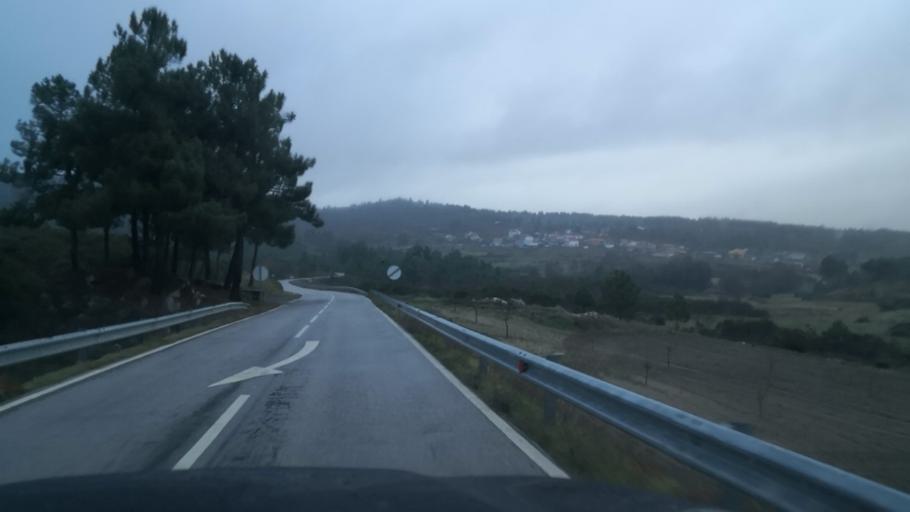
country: PT
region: Vila Real
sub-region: Murca
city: Murca
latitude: 41.4130
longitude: -7.5014
